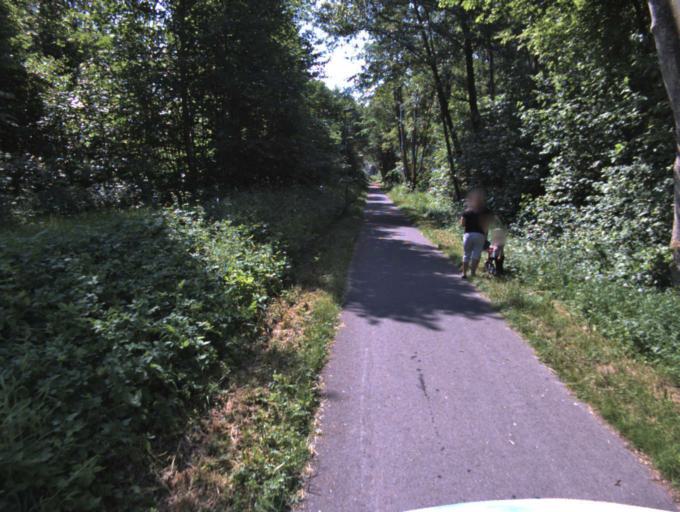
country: SE
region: Skane
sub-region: Kristianstads Kommun
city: Fjalkinge
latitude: 56.1006
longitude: 14.2468
